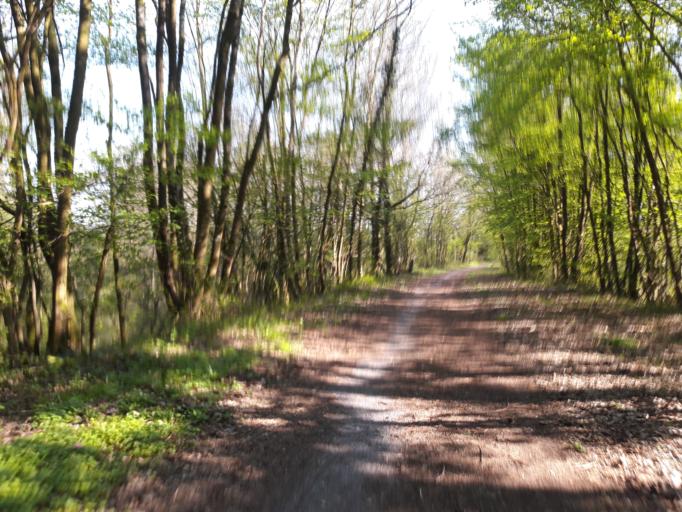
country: FR
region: Nord-Pas-de-Calais
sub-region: Departement du Nord
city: Sains-du-Nord
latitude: 50.1249
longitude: 4.0671
